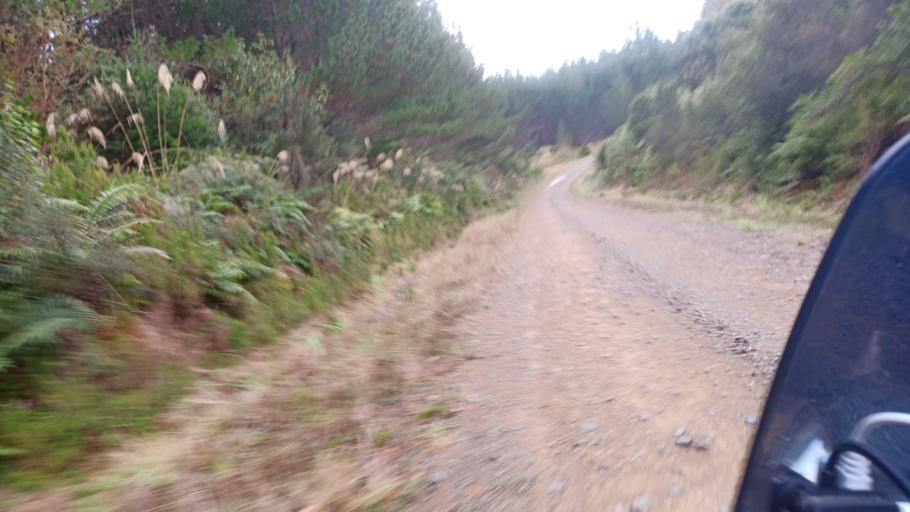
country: NZ
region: Bay of Plenty
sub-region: Whakatane District
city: Murupara
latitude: -38.6721
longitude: 176.6155
